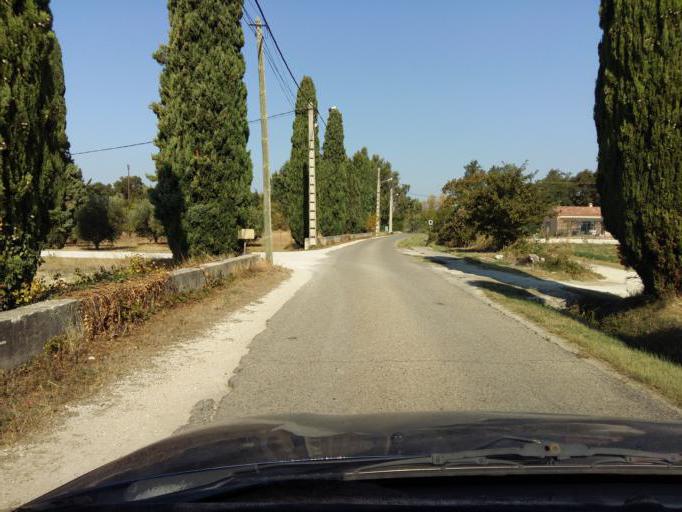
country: FR
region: Provence-Alpes-Cote d'Azur
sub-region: Departement du Vaucluse
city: Camaret-sur-Aigues
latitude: 44.1731
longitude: 4.8725
